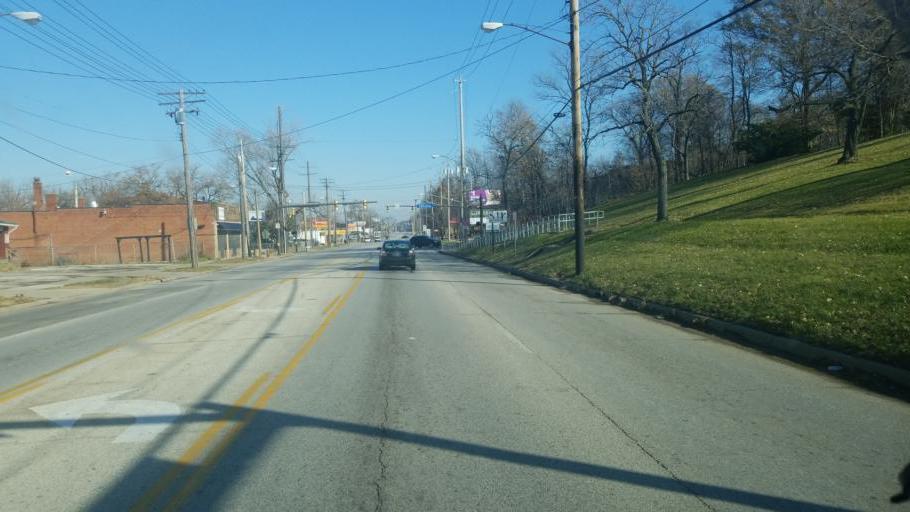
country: US
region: Ohio
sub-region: Cuyahoga County
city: East Cleveland
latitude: 41.5545
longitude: -81.5535
